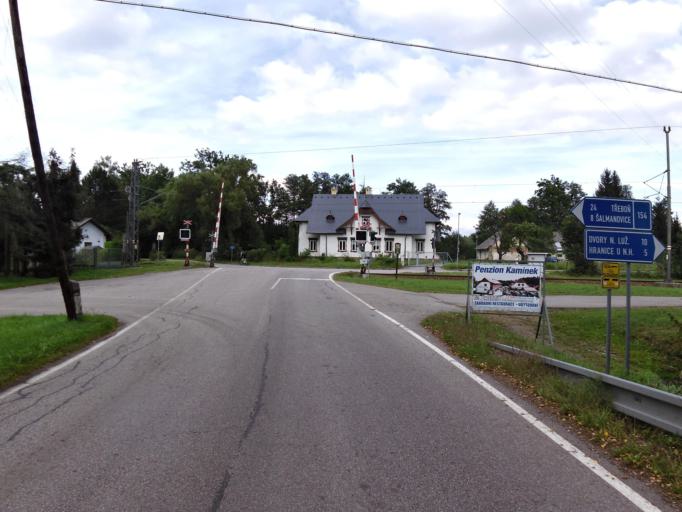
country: CZ
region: Jihocesky
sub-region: Okres Ceske Budejovice
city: Nove Hrady
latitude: 48.8240
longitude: 14.8043
